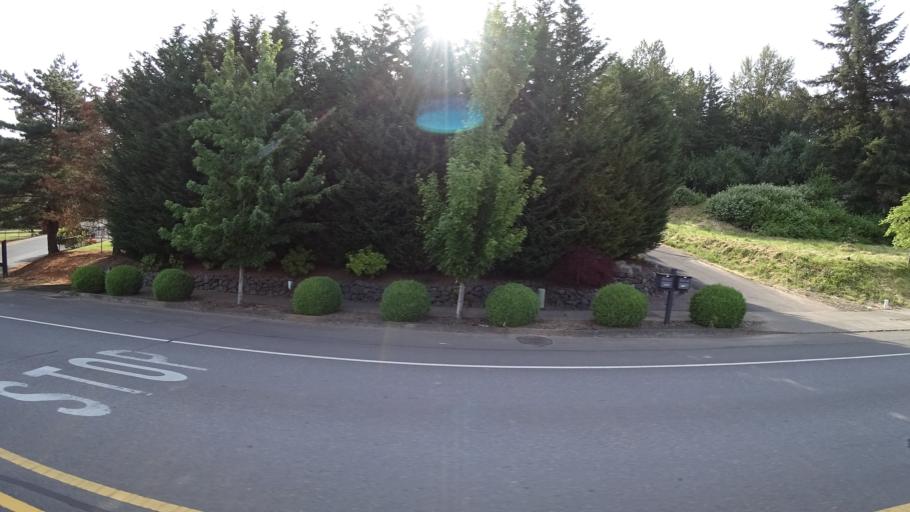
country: US
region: Oregon
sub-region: Clackamas County
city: Happy Valley
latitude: 45.4462
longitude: -122.5149
